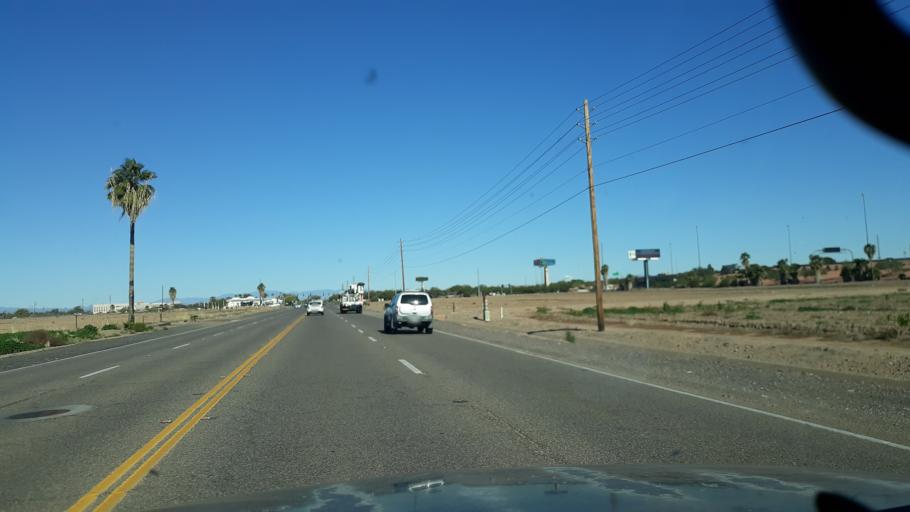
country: US
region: Arizona
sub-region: Maricopa County
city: Peoria
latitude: 33.5328
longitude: -112.2724
